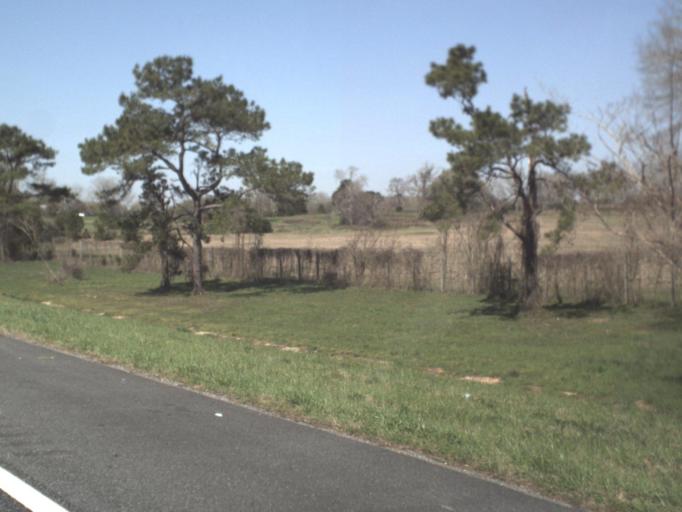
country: US
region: Florida
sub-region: Jackson County
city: Marianna
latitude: 30.7559
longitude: -85.3537
